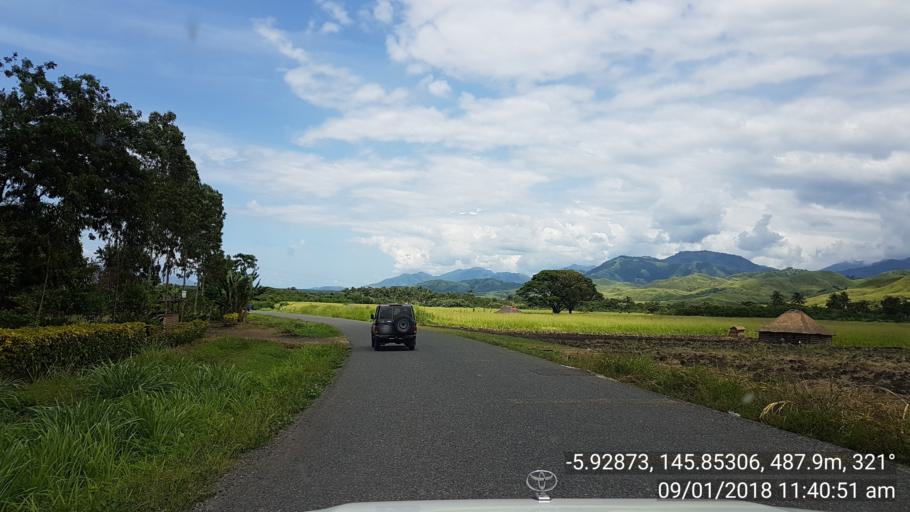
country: PG
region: Eastern Highlands
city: Kainantu
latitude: -5.9290
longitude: 145.8531
